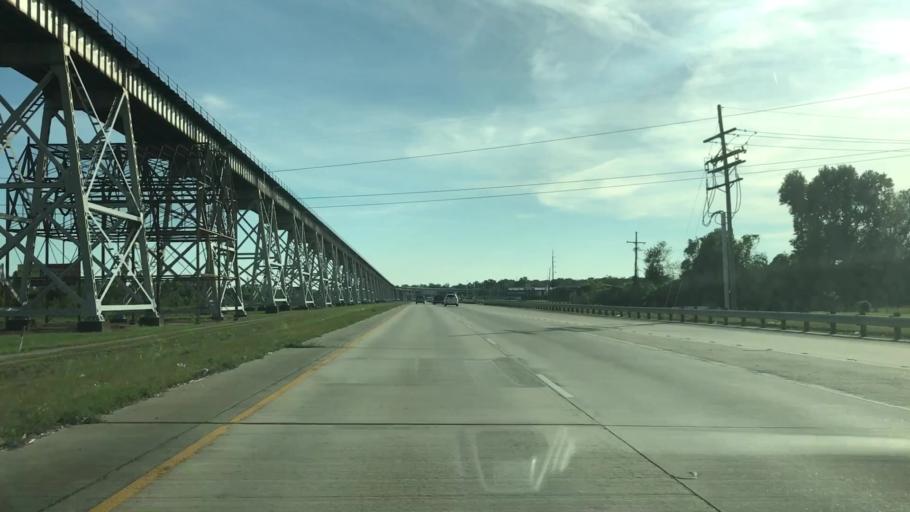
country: US
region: Louisiana
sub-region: Jefferson Parish
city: Bridge City
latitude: 29.9256
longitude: -90.1676
